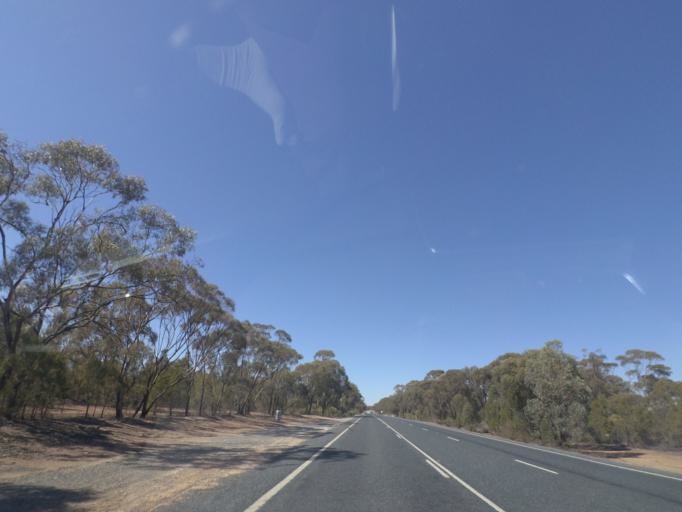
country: AU
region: New South Wales
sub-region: Bland
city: West Wyalong
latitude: -34.1306
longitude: 147.1237
